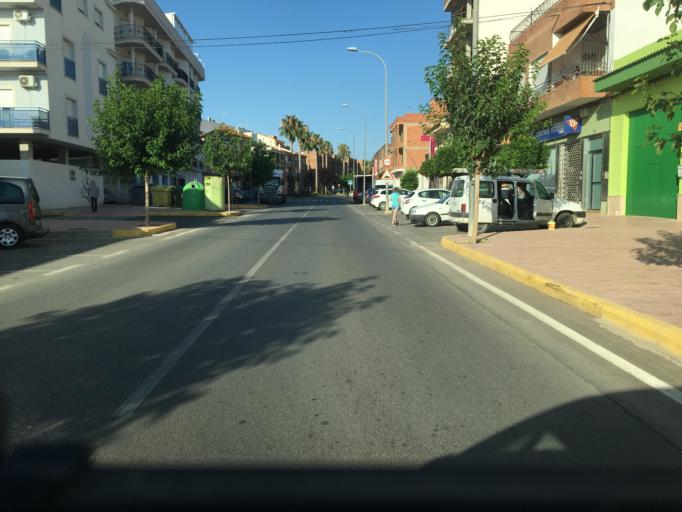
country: ES
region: Murcia
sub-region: Murcia
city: Puerto Lumbreras
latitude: 37.5647
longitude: -1.8038
